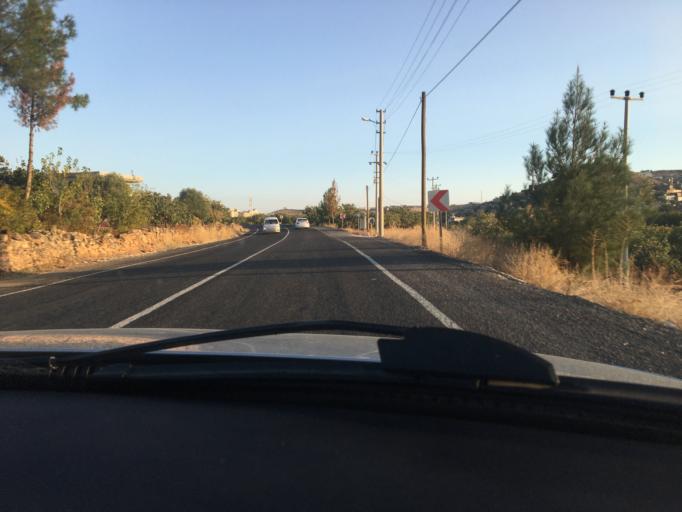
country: TR
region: Sanliurfa
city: Halfeti
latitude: 37.2170
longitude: 37.9550
